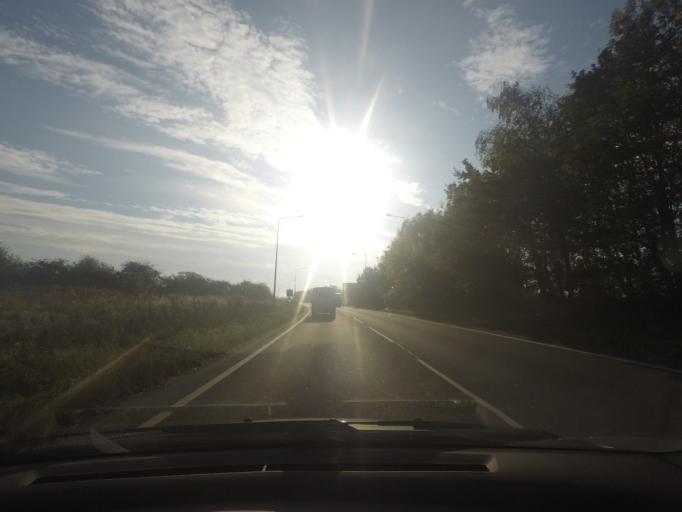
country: GB
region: England
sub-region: East Riding of Yorkshire
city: Market Weighton
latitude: 53.8601
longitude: -0.6804
